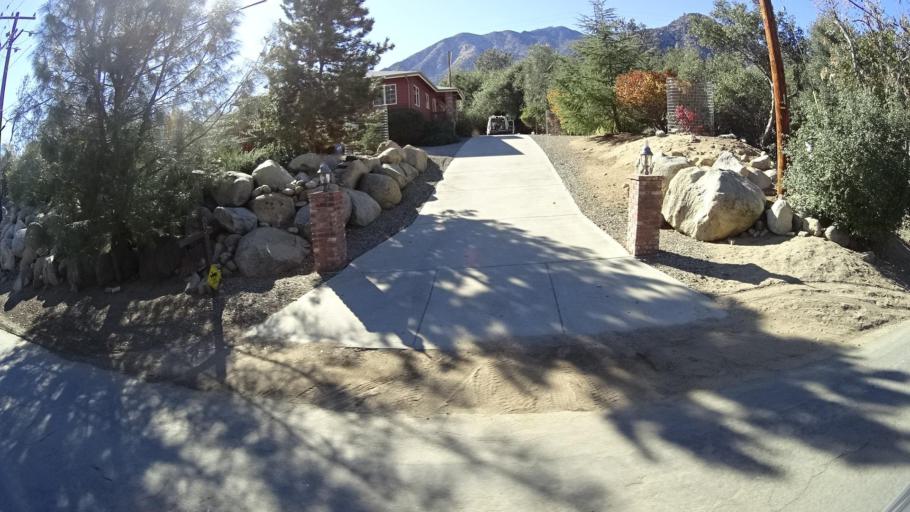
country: US
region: California
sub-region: Kern County
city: Kernville
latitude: 35.7675
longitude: -118.4336
